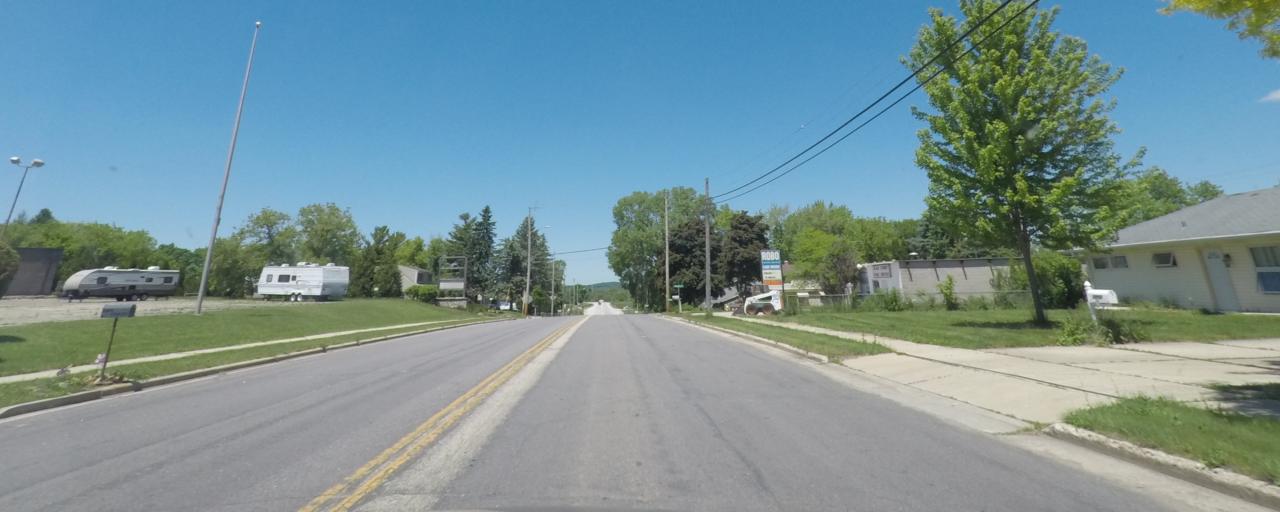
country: US
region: Wisconsin
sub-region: Washington County
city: West Bend
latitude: 43.4452
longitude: -88.1893
